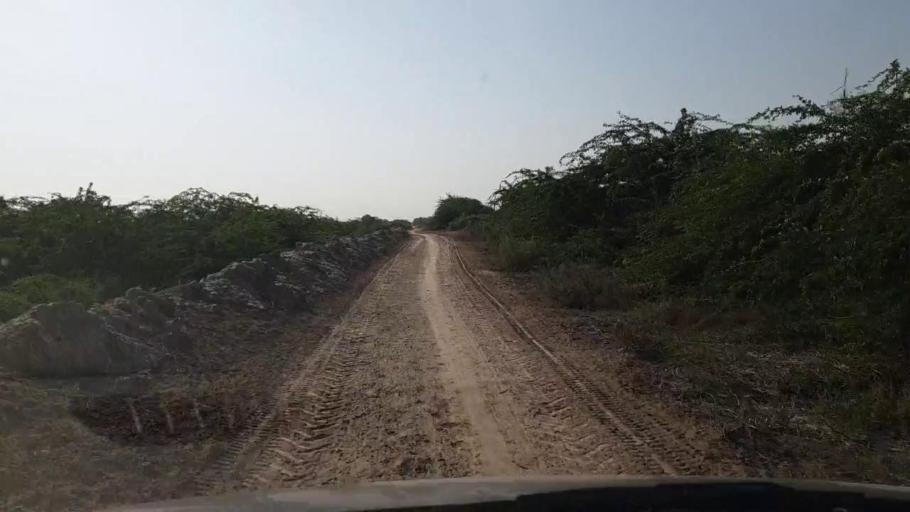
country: PK
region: Sindh
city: Kadhan
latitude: 24.6050
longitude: 69.0740
